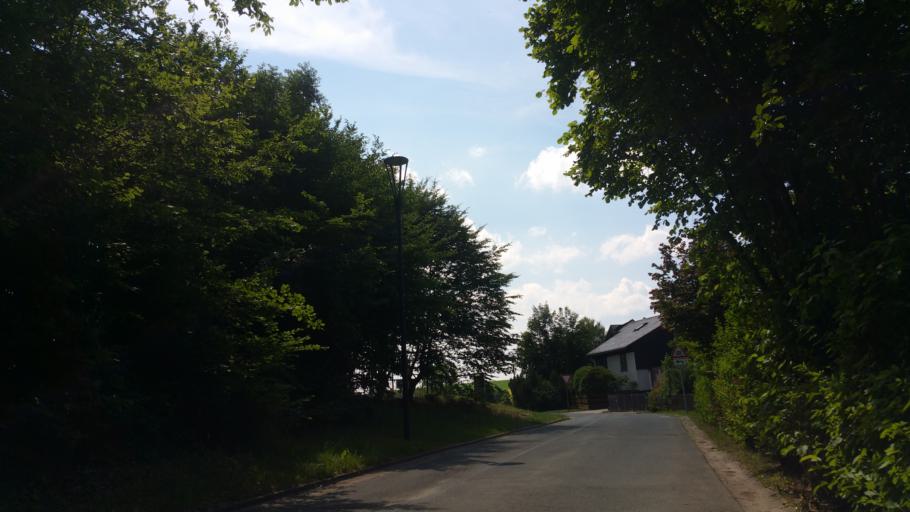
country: DE
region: Bavaria
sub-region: Upper Franconia
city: Schwarzenbach an der Saale
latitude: 50.2077
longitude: 11.9110
